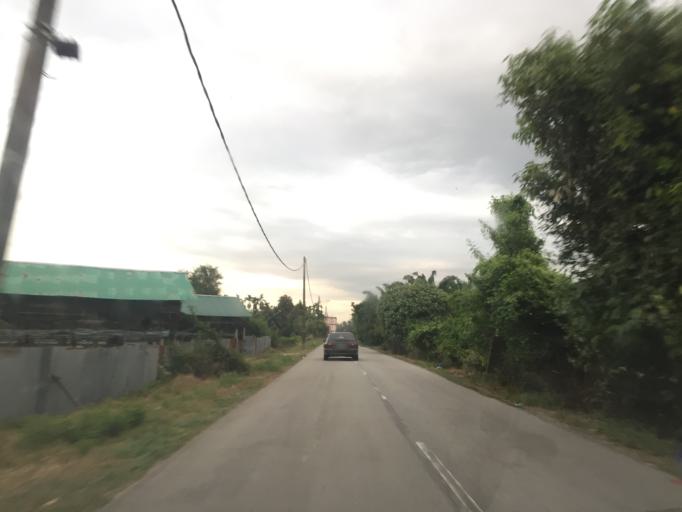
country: MY
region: Penang
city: Tasek Glugor
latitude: 5.5379
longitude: 100.5207
